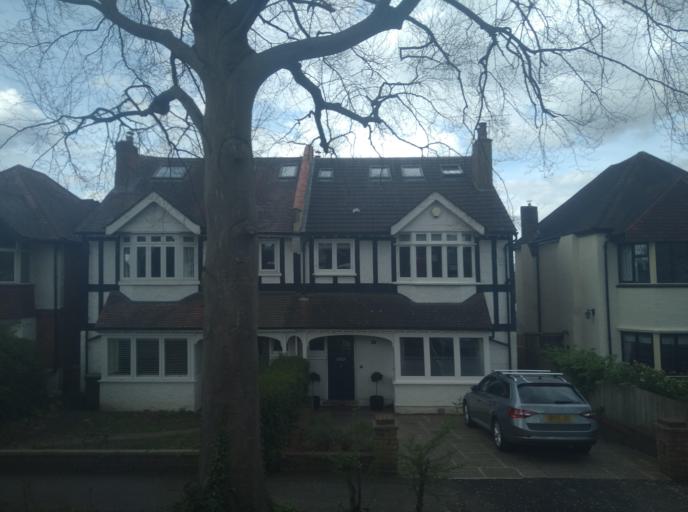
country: GB
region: England
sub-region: Greater London
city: Carshalton
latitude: 51.3552
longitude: -0.1709
